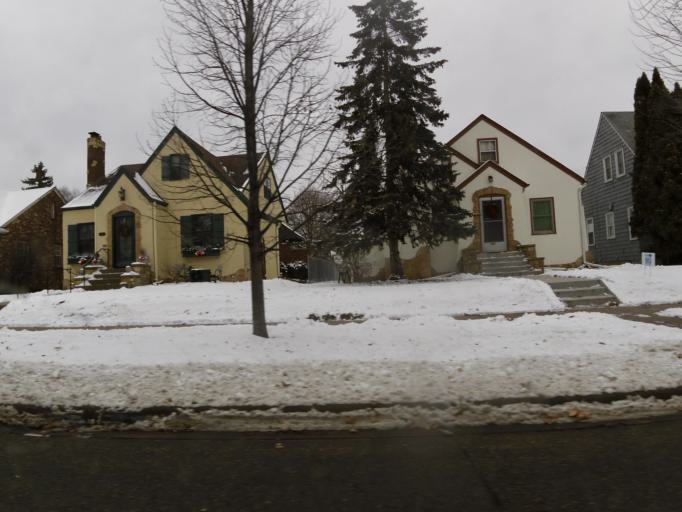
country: US
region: Minnesota
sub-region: Dakota County
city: Mendota Heights
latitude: 44.9305
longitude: -93.1492
